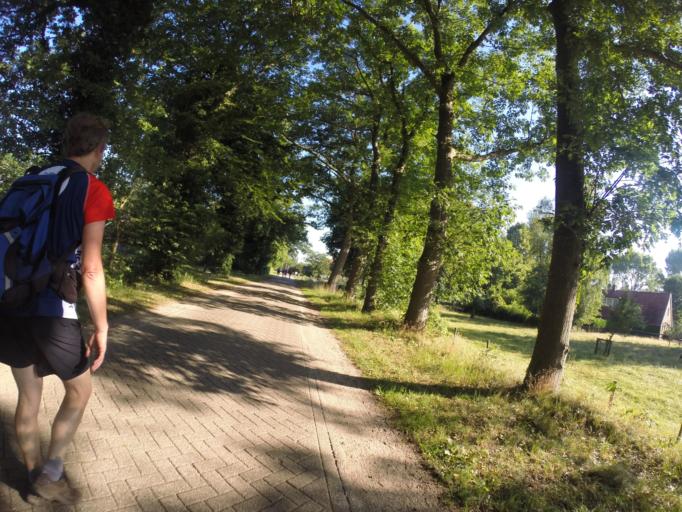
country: NL
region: Gelderland
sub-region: Gemeente Bronckhorst
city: Hengelo
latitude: 52.0978
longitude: 6.3629
